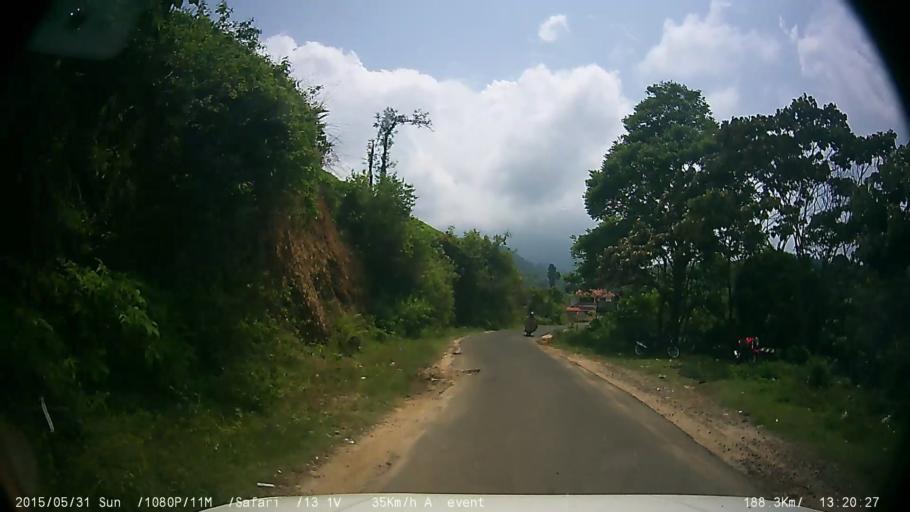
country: IN
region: Kerala
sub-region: Wayanad
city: Kalpetta
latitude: 11.5320
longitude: 76.1384
